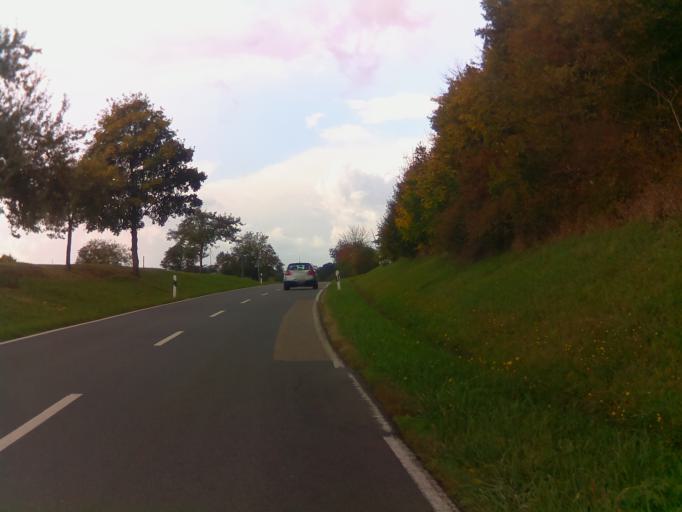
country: DE
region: Baden-Wuerttemberg
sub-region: Regierungsbezirk Stuttgart
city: Grossrinderfeld
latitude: 49.6667
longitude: 9.7572
